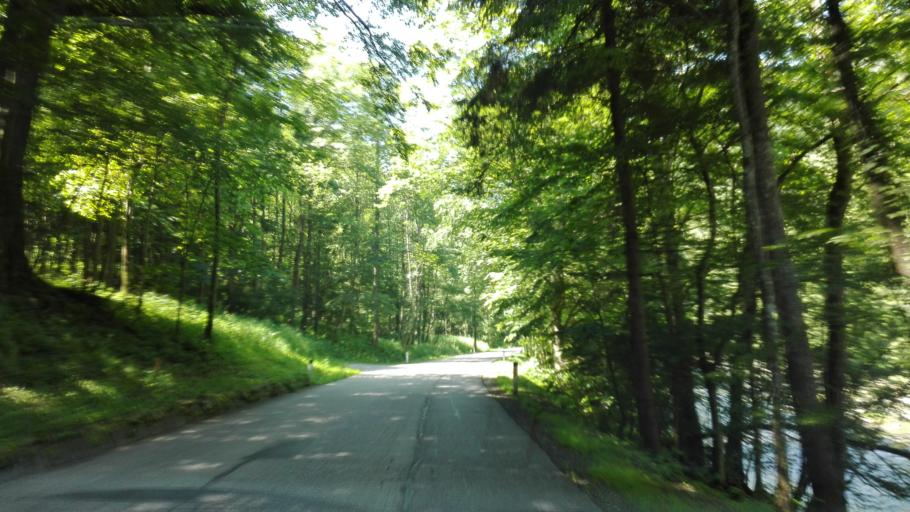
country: AT
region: Upper Austria
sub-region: Politischer Bezirk Rohrbach
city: Kleinzell im Muehlkreis
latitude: 48.3773
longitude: 13.9345
